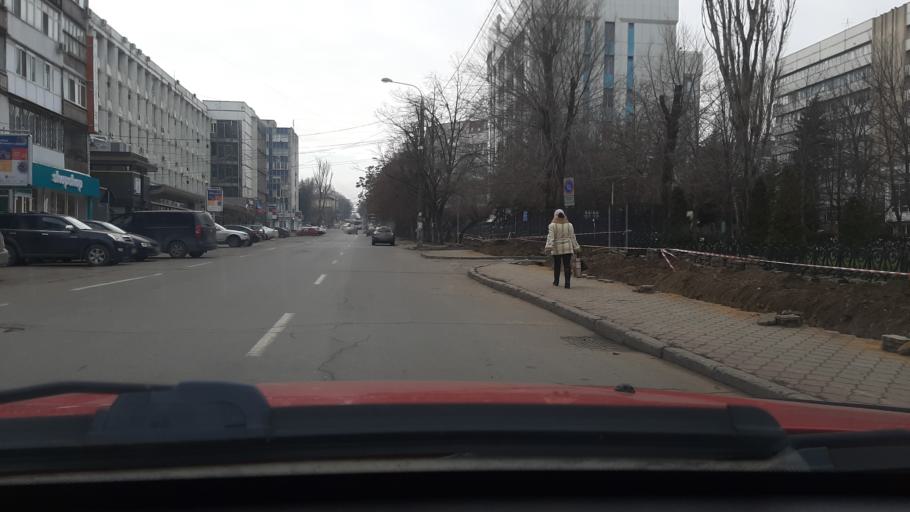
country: MD
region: Chisinau
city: Chisinau
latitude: 47.0306
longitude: 28.8382
